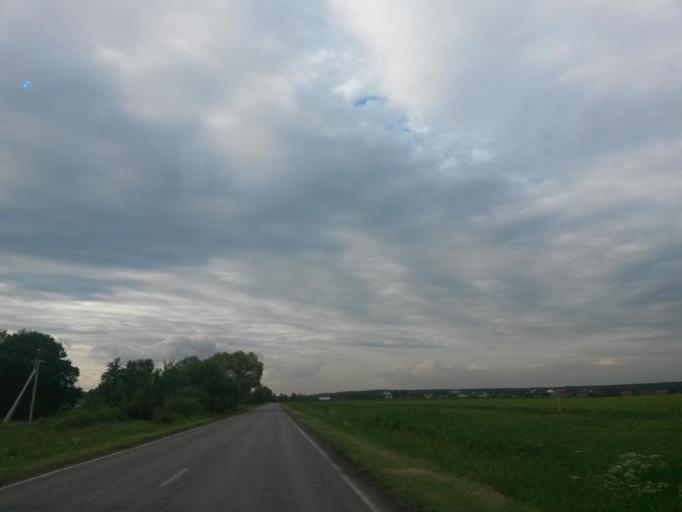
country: RU
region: Moskovskaya
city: Lyubuchany
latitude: 55.2400
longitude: 37.6422
